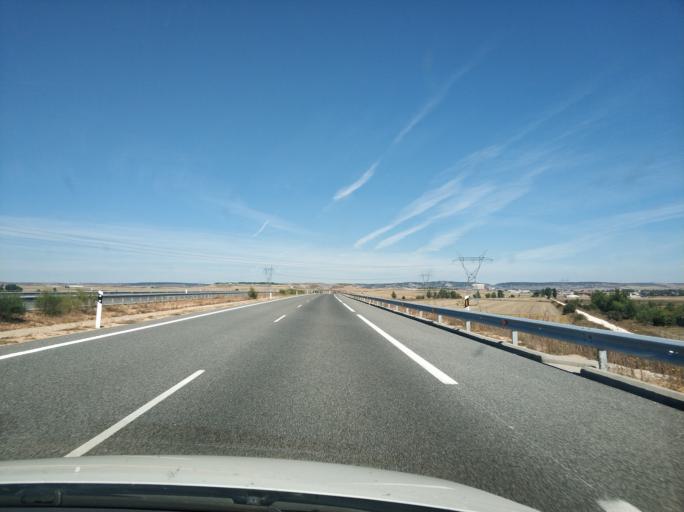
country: ES
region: Castille and Leon
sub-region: Provincia de Burgos
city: Sotragero
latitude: 42.4168
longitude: -3.6965
